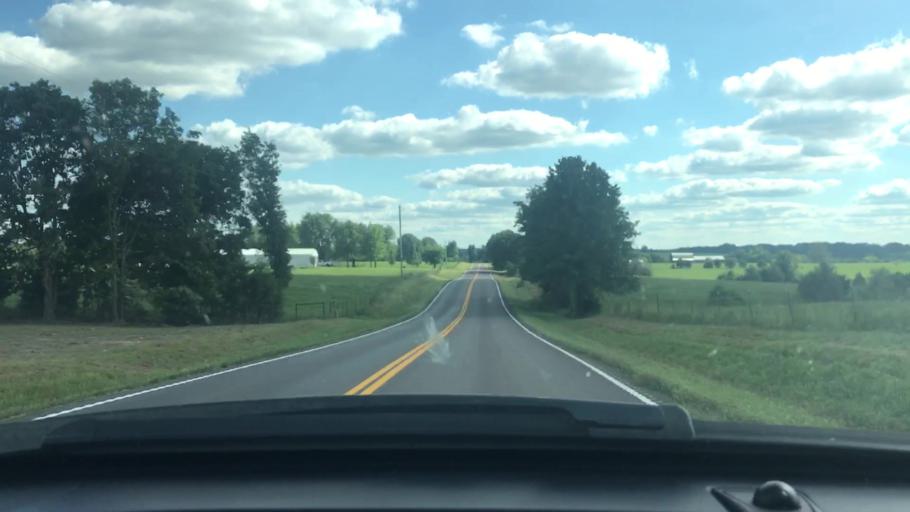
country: US
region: Missouri
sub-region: Wright County
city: Mountain Grove
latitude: 37.2618
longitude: -92.3081
